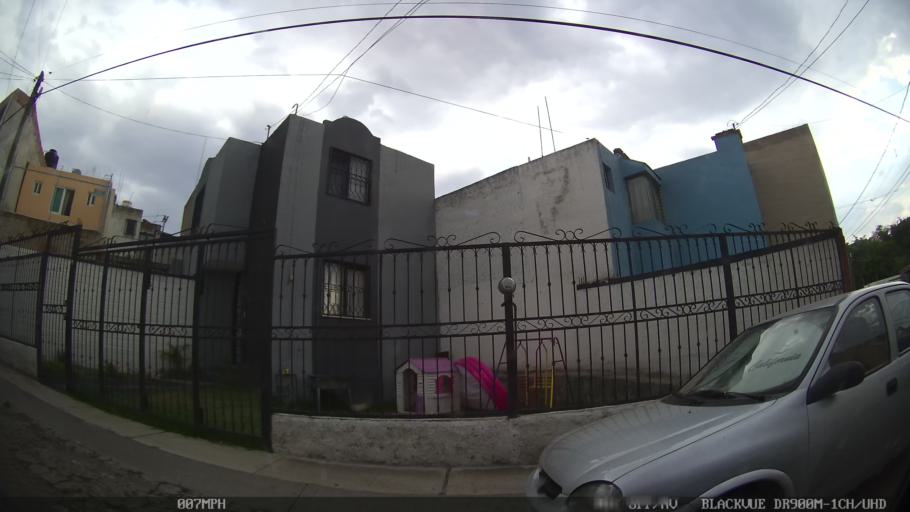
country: MX
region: Jalisco
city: Tlaquepaque
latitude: 20.6256
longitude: -103.2793
